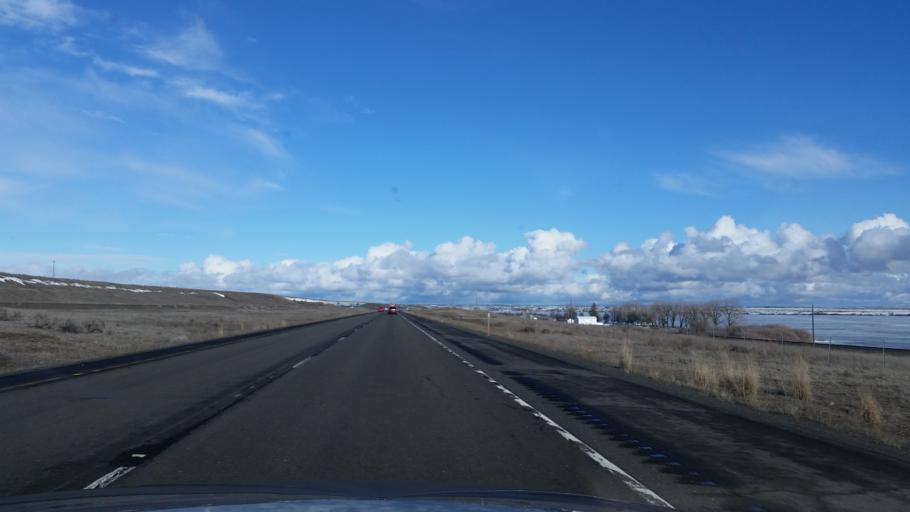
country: US
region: Washington
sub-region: Adams County
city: Ritzville
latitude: 47.2536
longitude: -118.0947
